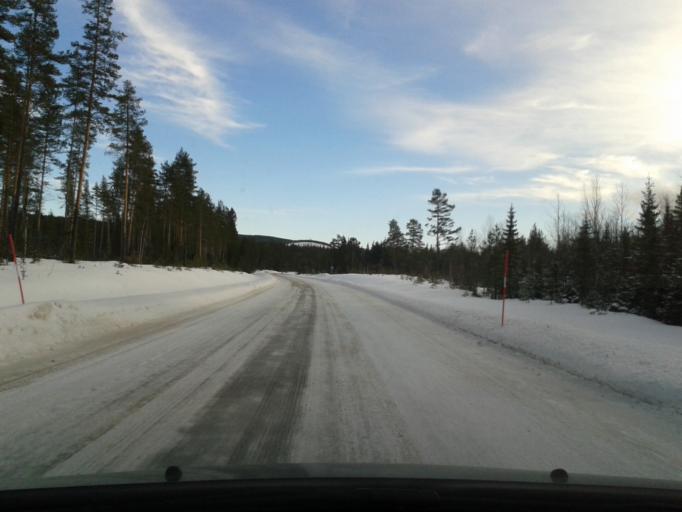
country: SE
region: Vaesterbotten
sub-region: Asele Kommun
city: Asele
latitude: 64.2776
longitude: 17.2689
